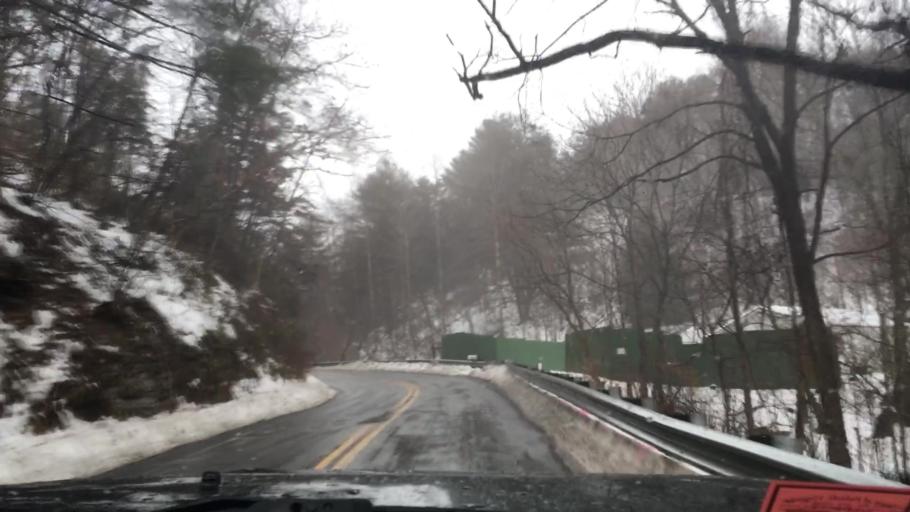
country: US
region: Virginia
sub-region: Pulaski County
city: Dublin
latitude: 37.0031
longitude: -80.6718
